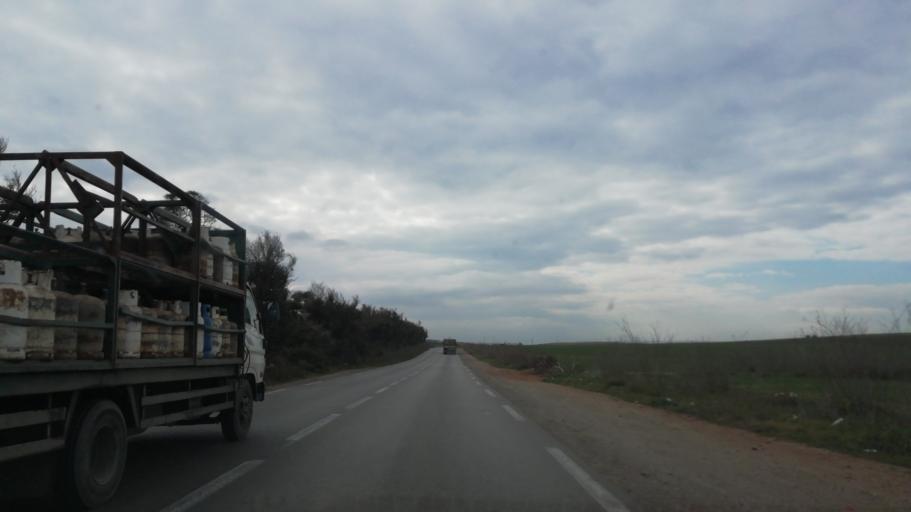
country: DZ
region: Oran
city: Ain el Bya
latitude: 35.7616
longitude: -0.3496
